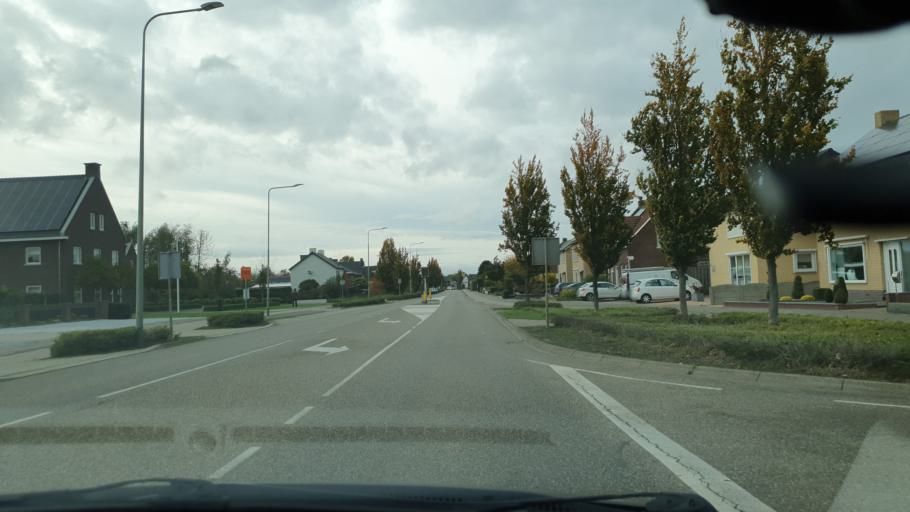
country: NL
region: Limburg
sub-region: Gemeente Roerdalen
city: Montfort
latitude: 51.0910
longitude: 5.9086
